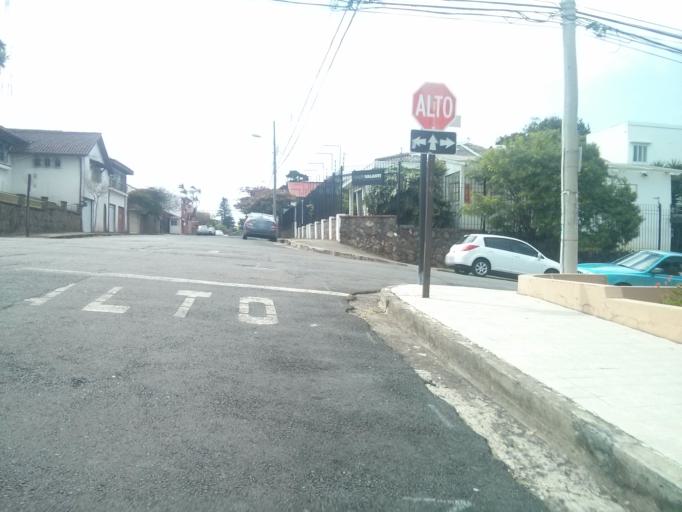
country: CR
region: San Jose
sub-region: Canton de Goicoechea
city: Guadalupe
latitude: 9.9366
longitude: -84.0620
